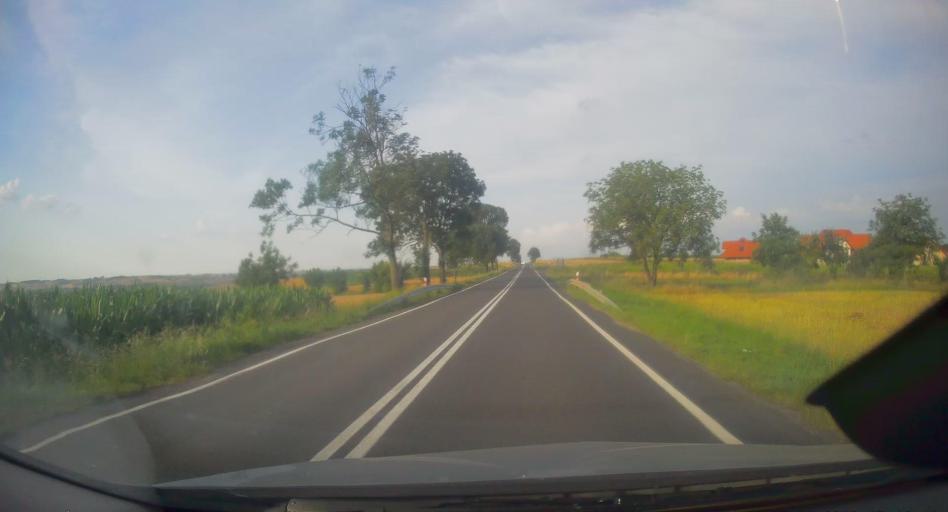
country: PL
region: Lesser Poland Voivodeship
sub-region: Powiat bochenski
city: Dziewin
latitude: 50.1514
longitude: 20.5251
